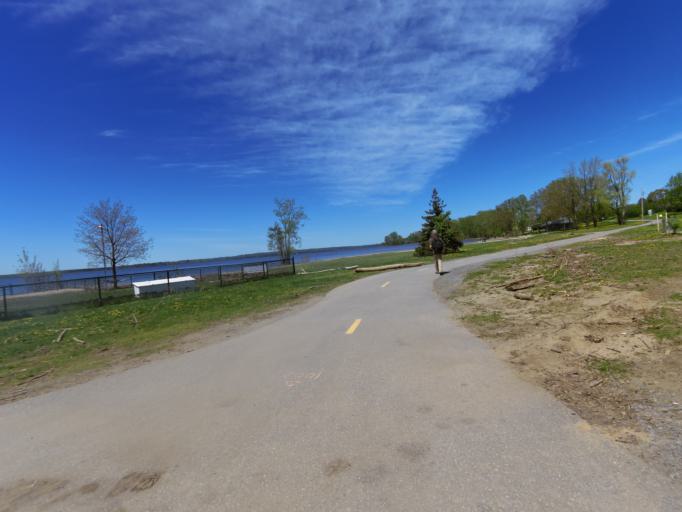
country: CA
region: Ontario
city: Bells Corners
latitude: 45.3963
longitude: -75.8585
